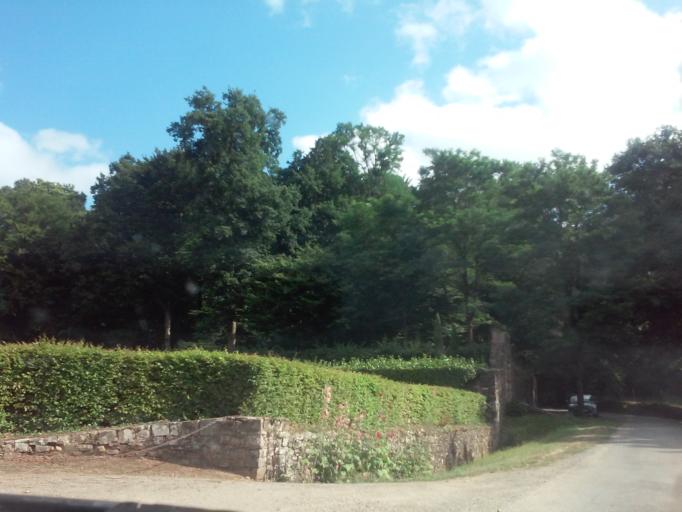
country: FR
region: Brittany
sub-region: Departement d'Ille-et-Vilaine
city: Bourg-des-Comptes
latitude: 47.9136
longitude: -1.7581
